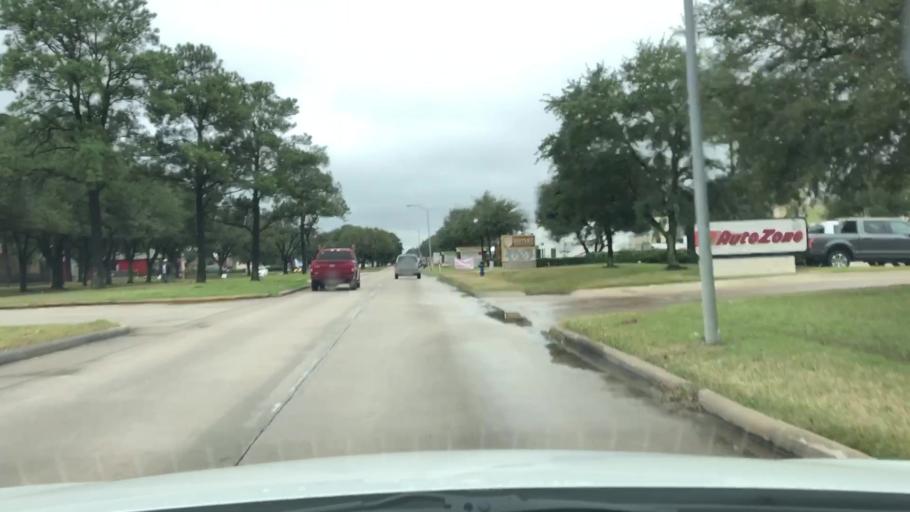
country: US
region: Texas
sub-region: Fort Bend County
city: Cinco Ranch
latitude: 29.7628
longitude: -95.7518
